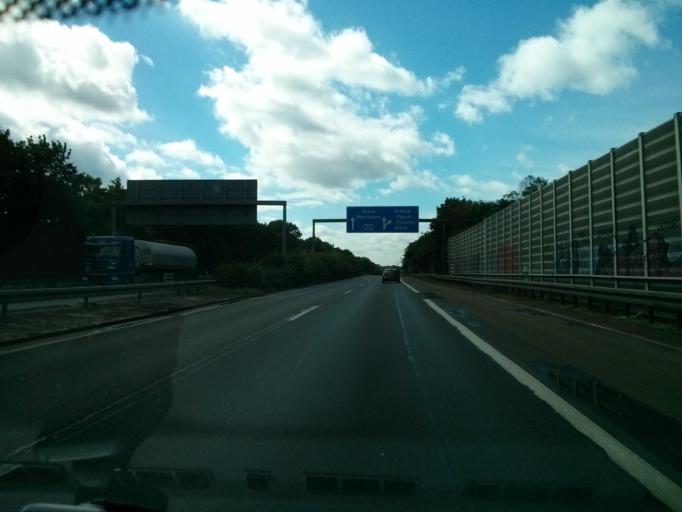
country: DE
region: North Rhine-Westphalia
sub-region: Regierungsbezirk Dusseldorf
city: Krefeld
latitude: 51.3334
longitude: 6.6268
